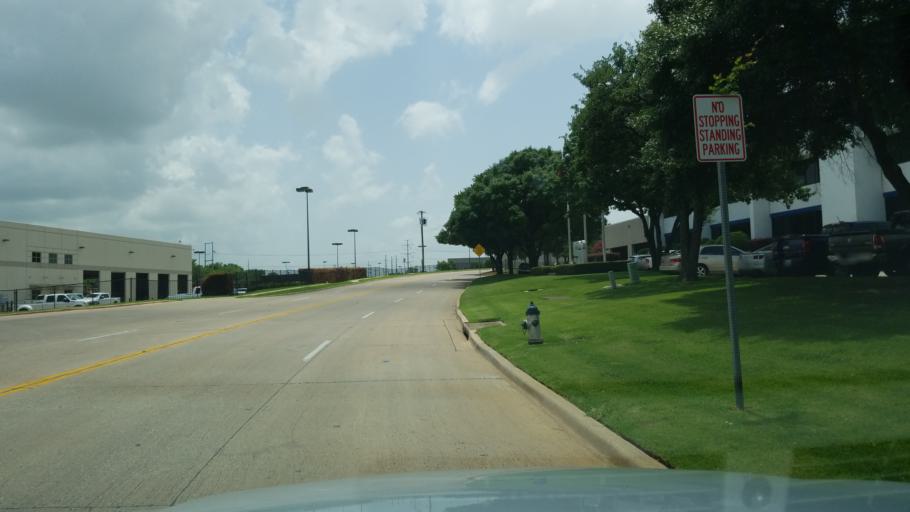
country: US
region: Texas
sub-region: Dallas County
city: Irving
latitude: 32.8195
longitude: -96.9093
